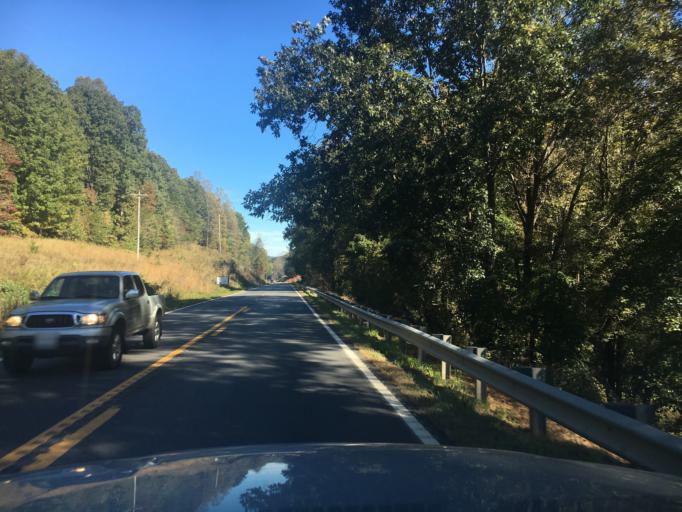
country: US
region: North Carolina
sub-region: Burke County
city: Glen Alpine
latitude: 35.6218
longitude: -81.8058
